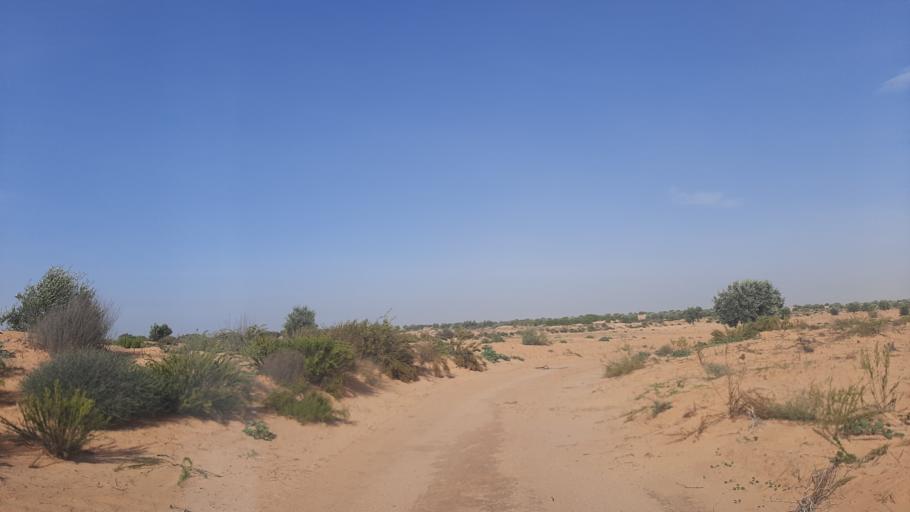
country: TN
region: Madanin
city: Zarzis
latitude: 33.4532
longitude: 10.8086
